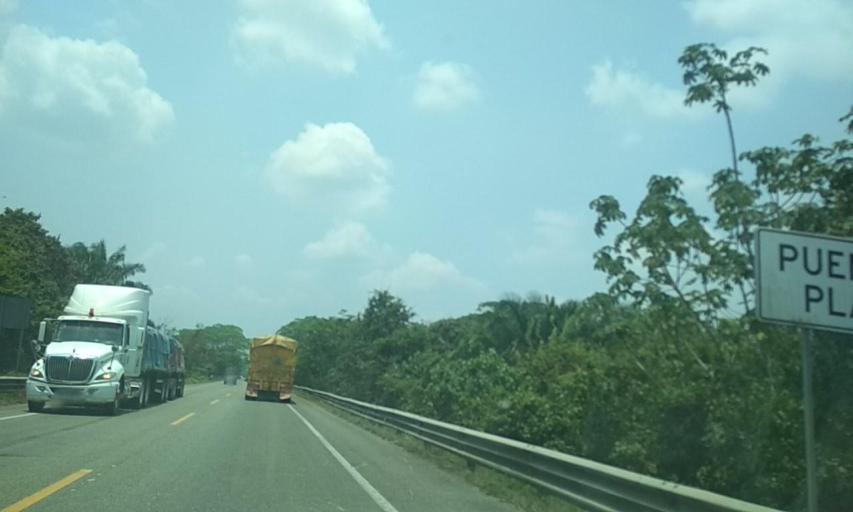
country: MX
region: Tabasco
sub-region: Huimanguillo
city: Francisco Rueda
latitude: 17.7349
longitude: -93.9736
